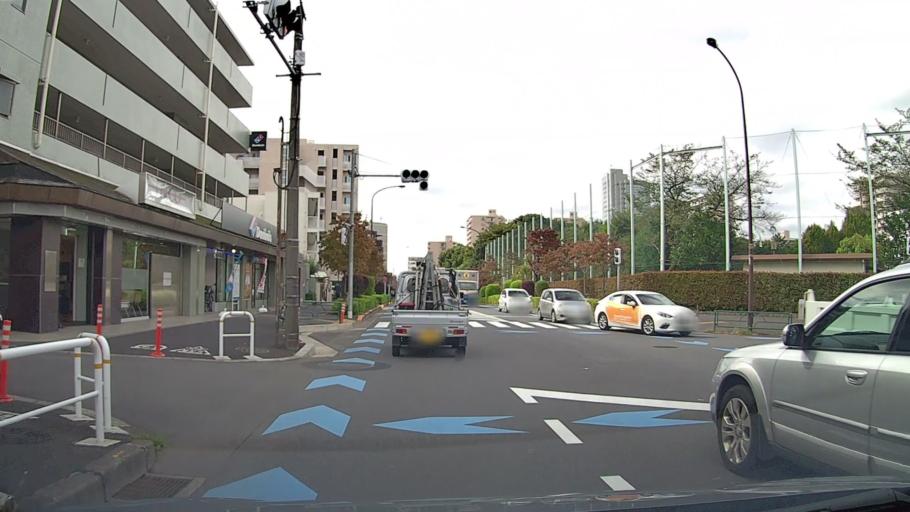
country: JP
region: Saitama
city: Wako
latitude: 35.7537
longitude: 139.6268
